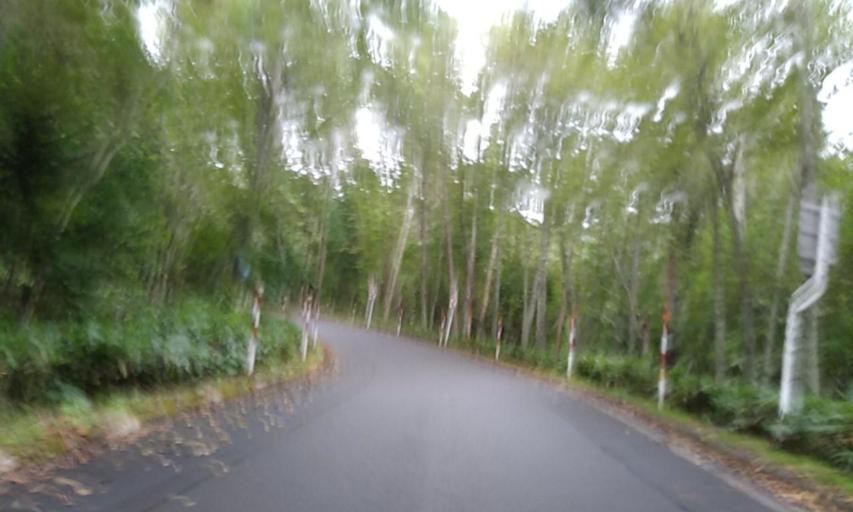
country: JP
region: Hokkaido
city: Bihoro
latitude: 43.5809
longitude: 144.2567
